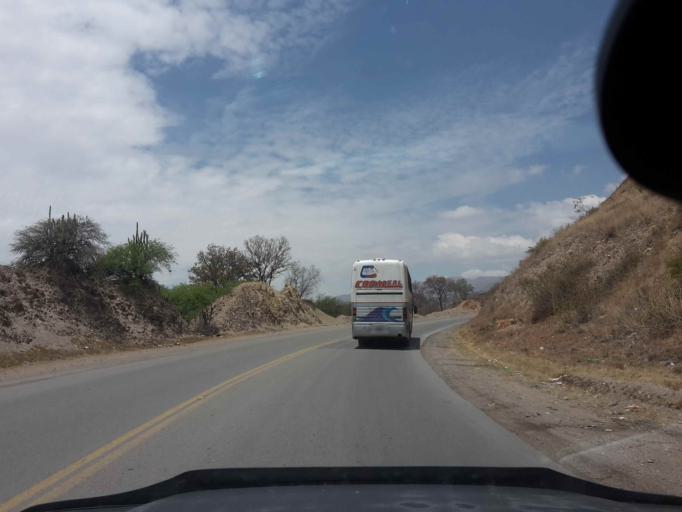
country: BO
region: Cochabamba
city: Sipe Sipe
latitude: -17.5482
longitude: -66.3407
